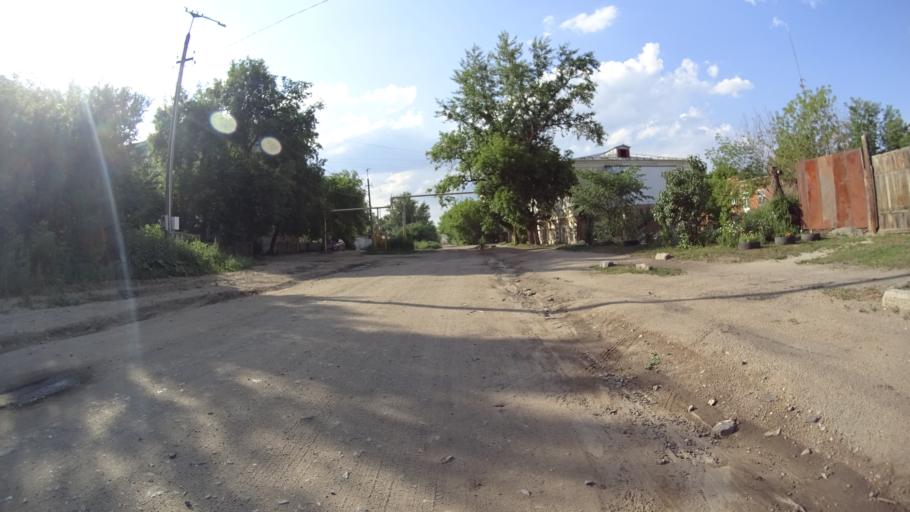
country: RU
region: Chelyabinsk
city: Troitsk
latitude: 54.0861
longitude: 61.5445
